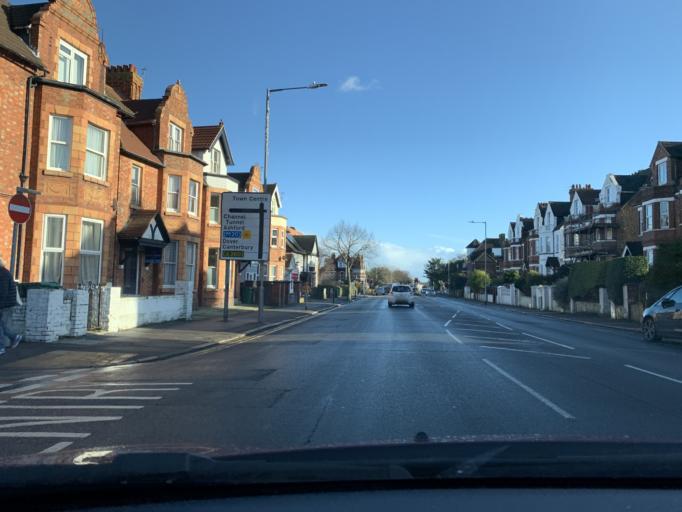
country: GB
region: England
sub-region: Kent
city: Hawkinge
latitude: 51.0862
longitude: 1.1537
